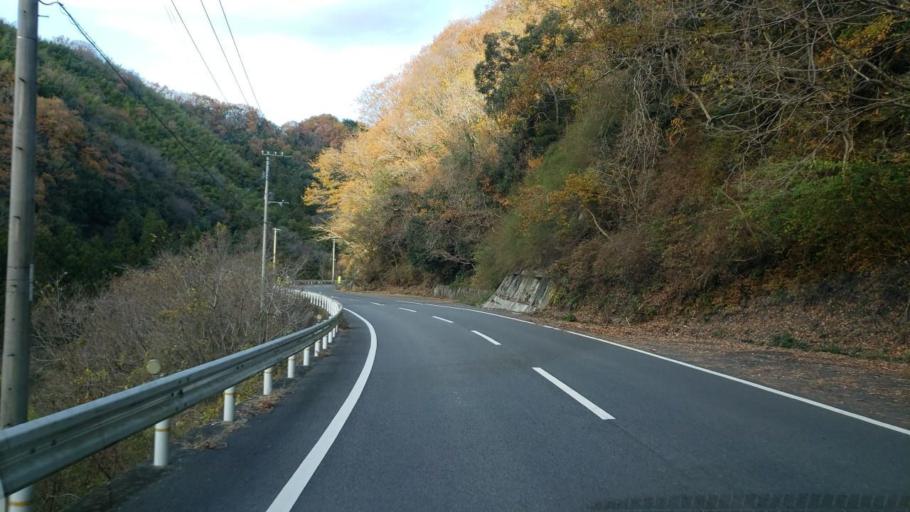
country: JP
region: Tokushima
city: Wakimachi
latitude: 34.1684
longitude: 134.0766
